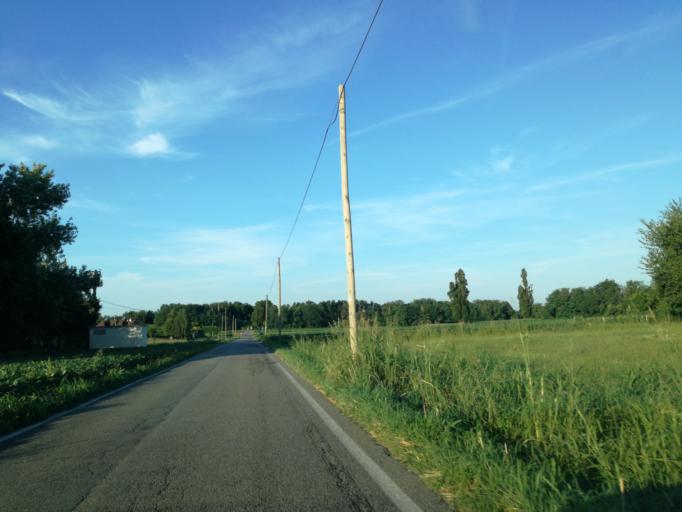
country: IT
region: Lombardy
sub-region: Provincia di Lecco
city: Verderio Inferiore
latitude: 45.6580
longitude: 9.4315
